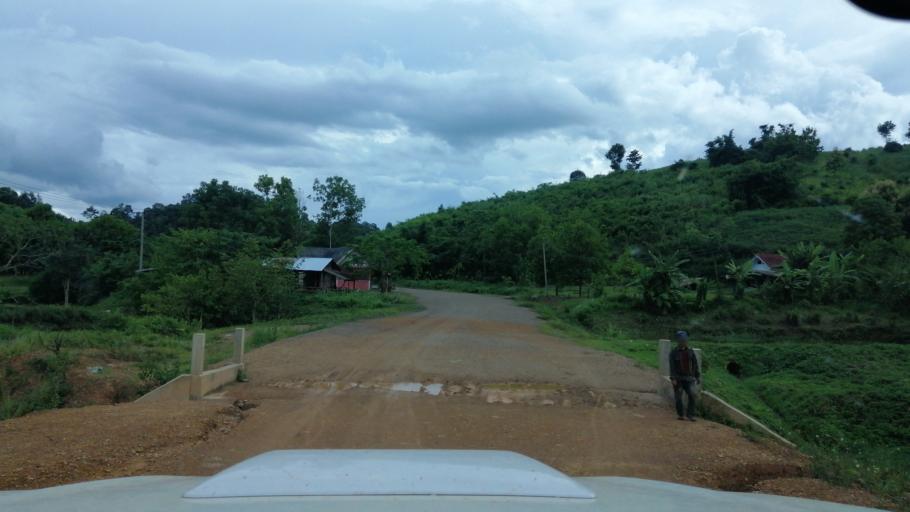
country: TH
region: Nan
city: Song Khwae
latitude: 19.5437
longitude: 100.7005
